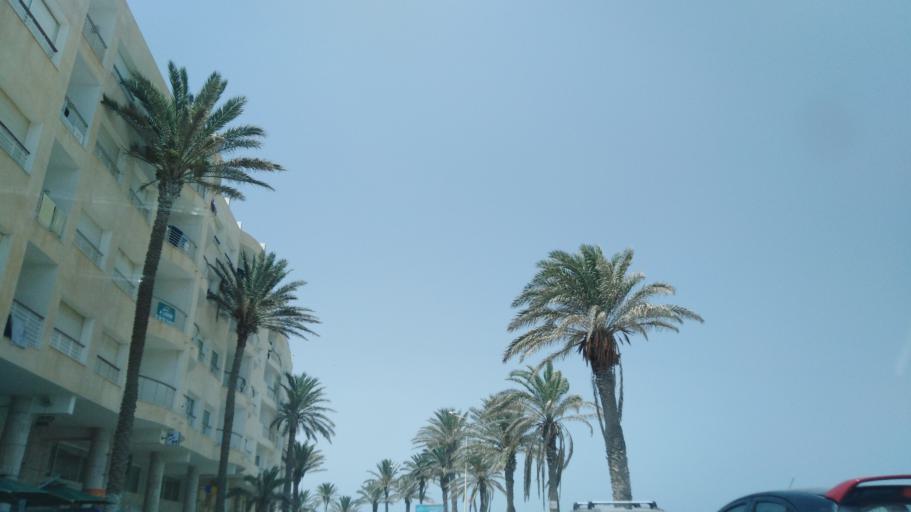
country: TN
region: Al Mahdiyah
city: Mahdia
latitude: 35.5223
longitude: 11.0417
